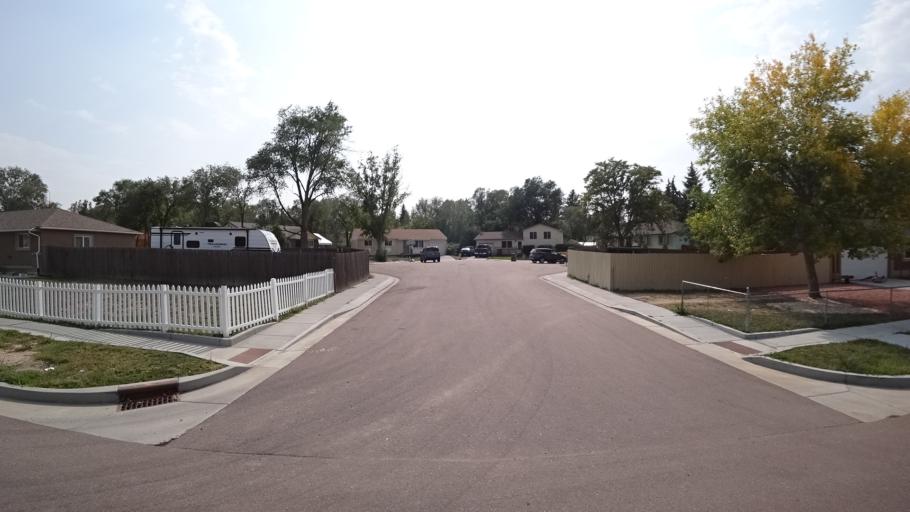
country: US
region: Colorado
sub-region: El Paso County
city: Stratmoor
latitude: 38.8280
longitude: -104.7522
